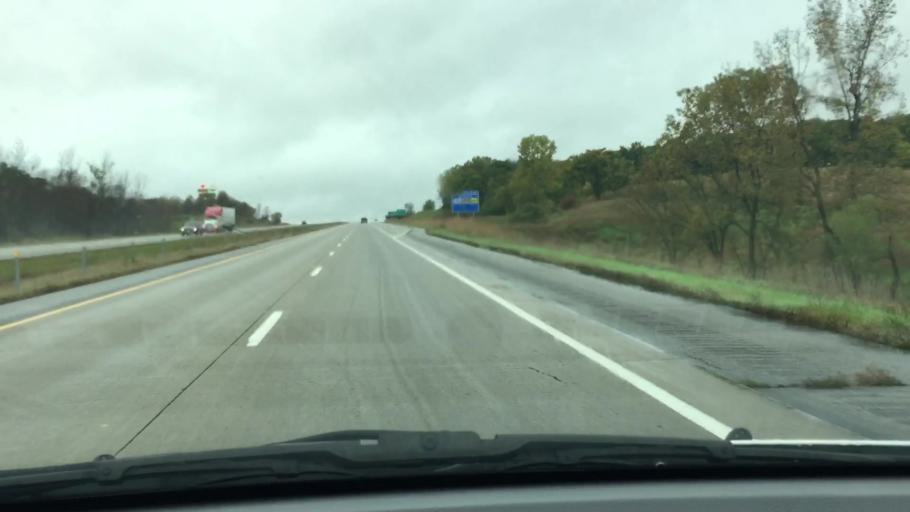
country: US
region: Iowa
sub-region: Jasper County
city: Newton
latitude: 41.6822
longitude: -92.9875
